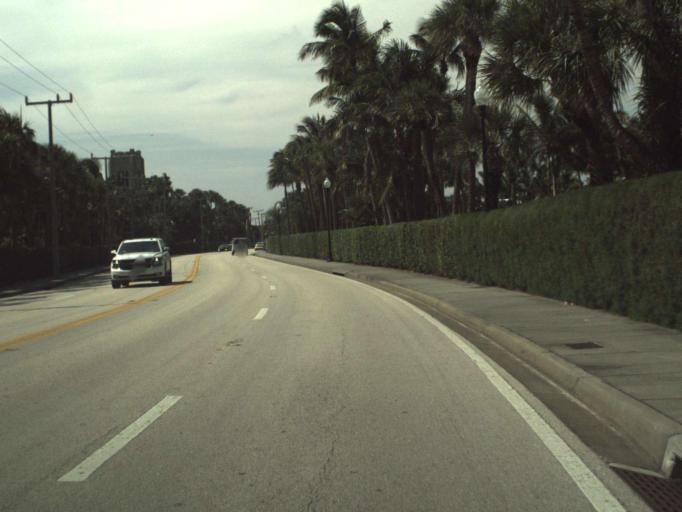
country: US
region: Florida
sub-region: Palm Beach County
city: Palm Beach
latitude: 26.7135
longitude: -80.0378
